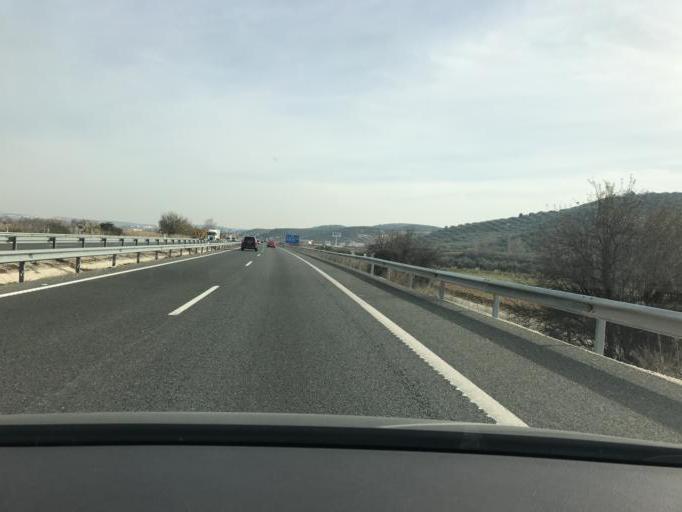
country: ES
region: Andalusia
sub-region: Provincia de Granada
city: Huetor-Tajar
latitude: 37.1802
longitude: -4.0693
